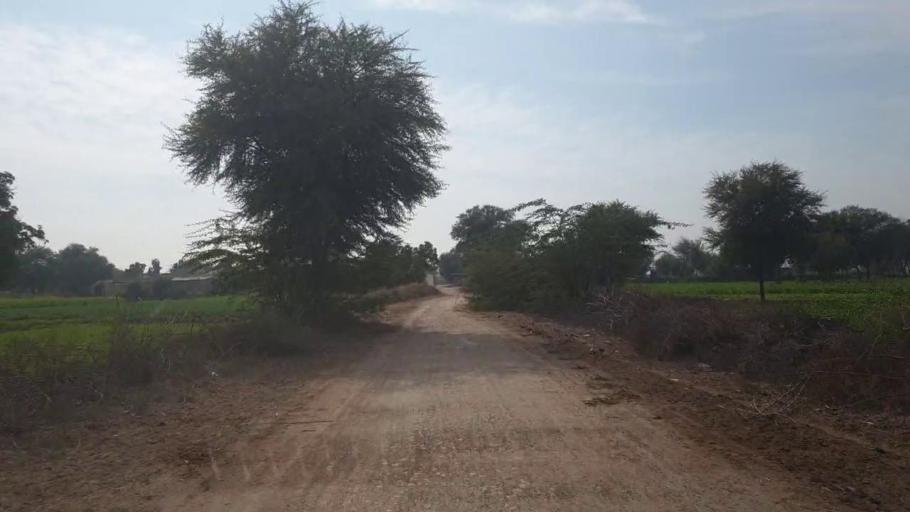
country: PK
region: Sindh
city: Nawabshah
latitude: 26.1204
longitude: 68.4738
